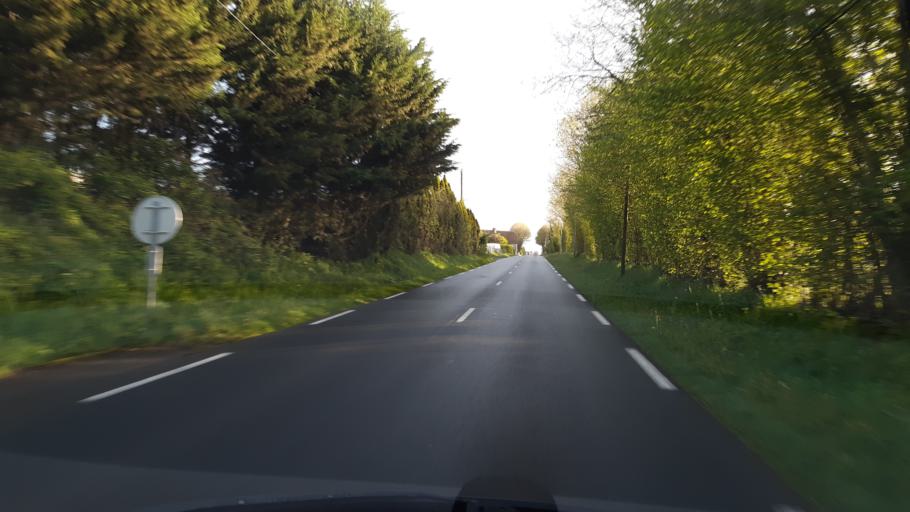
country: FR
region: Lower Normandy
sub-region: Departement de la Manche
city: Tessy-sur-Vire
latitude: 49.0229
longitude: -1.1462
